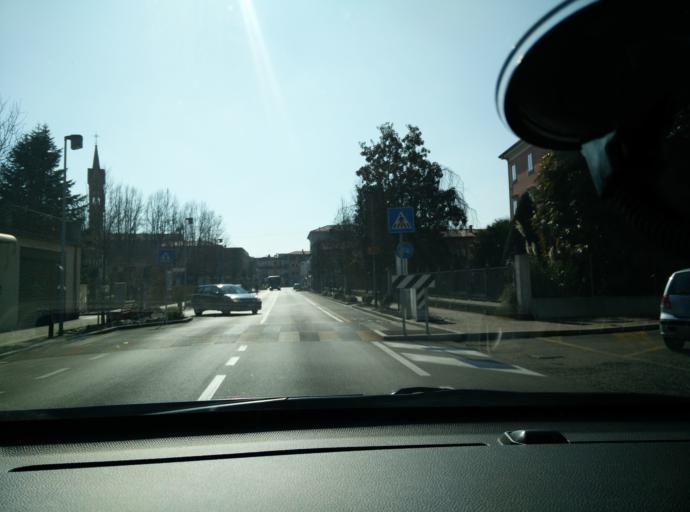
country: IT
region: Veneto
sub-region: Provincia di Venezia
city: San Dona di Piave
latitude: 45.6235
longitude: 12.5633
